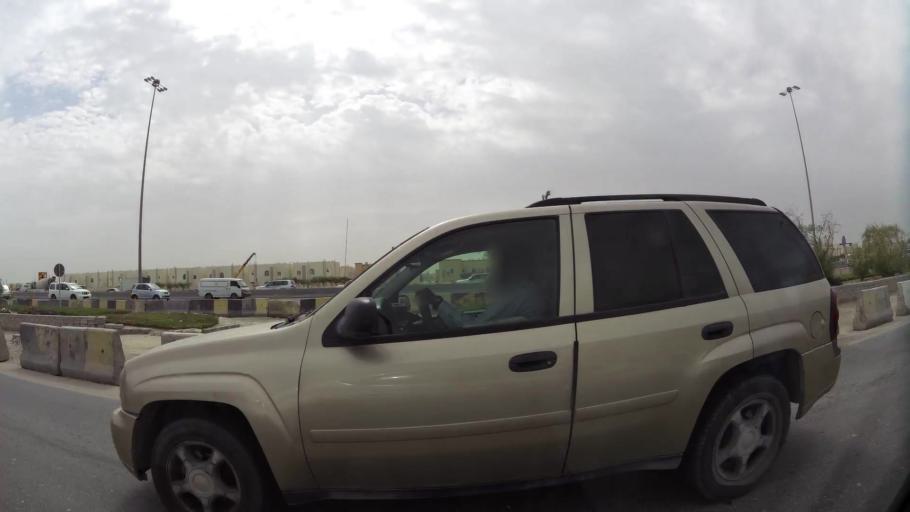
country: QA
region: Baladiyat ar Rayyan
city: Ar Rayyan
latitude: 25.3489
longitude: 51.4563
